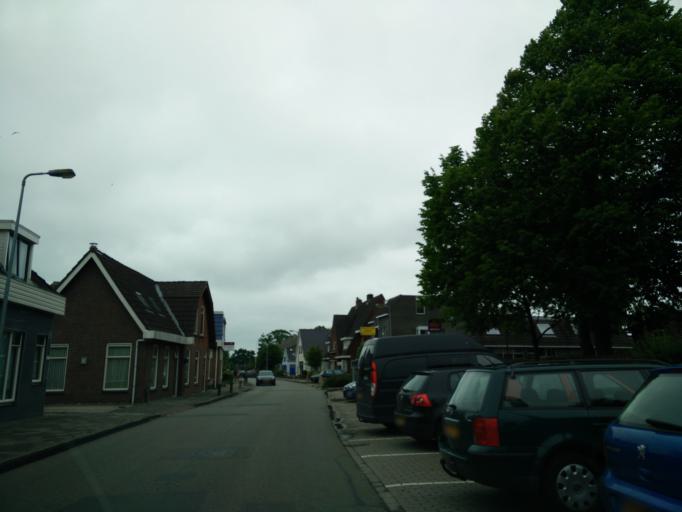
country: NL
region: Groningen
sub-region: Gemeente Zuidhorn
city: Aduard
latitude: 53.2164
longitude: 6.5005
